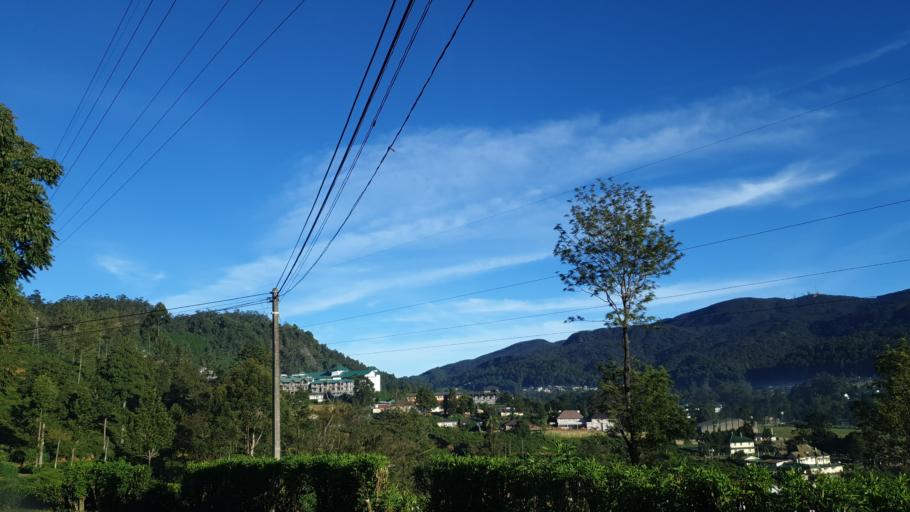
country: LK
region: Central
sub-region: Nuwara Eliya District
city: Nuwara Eliya
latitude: 6.9572
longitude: 80.7671
